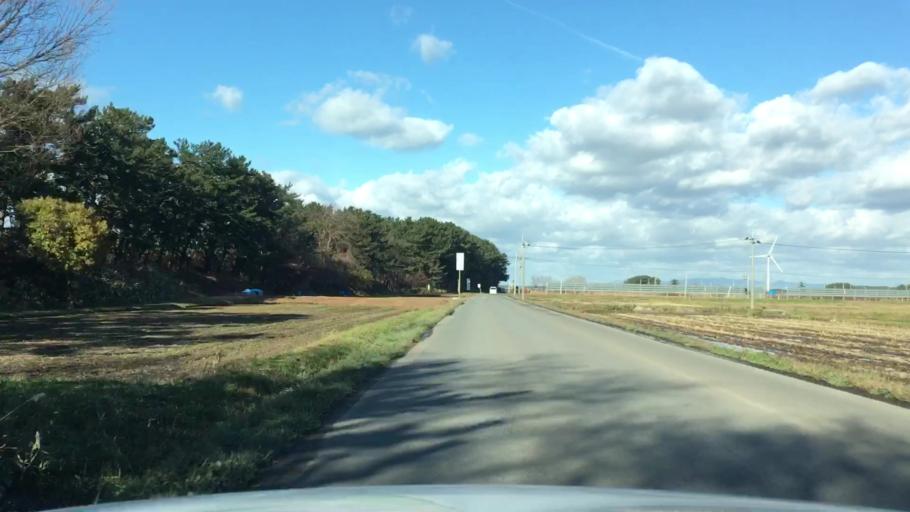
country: JP
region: Aomori
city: Shimokizukuri
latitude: 40.8472
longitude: 140.2998
